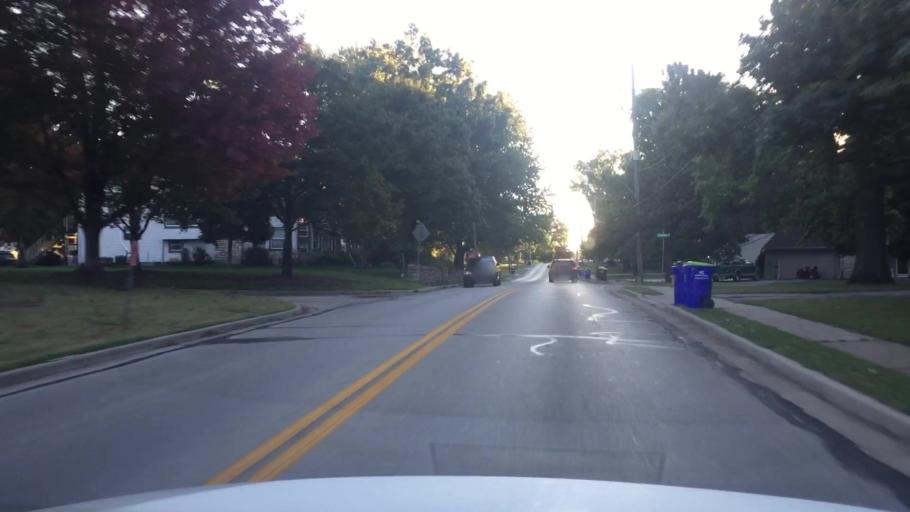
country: US
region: Kansas
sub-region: Johnson County
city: Shawnee
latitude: 39.0294
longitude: -94.7132
